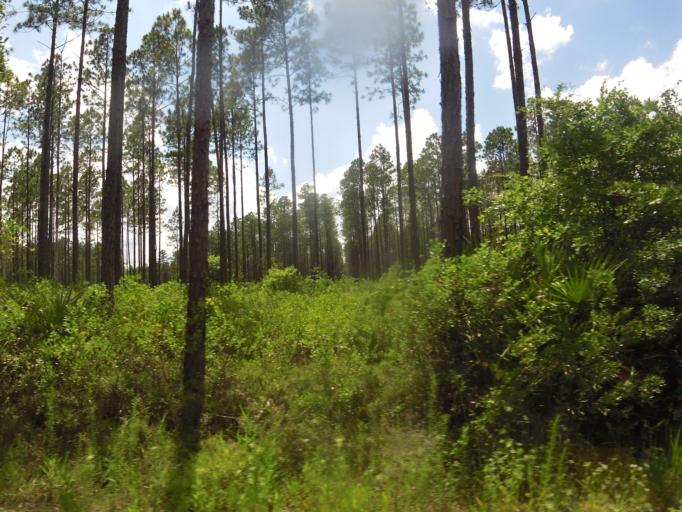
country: US
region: Florida
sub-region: Clay County
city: Asbury Lake
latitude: 29.8806
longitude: -81.8527
